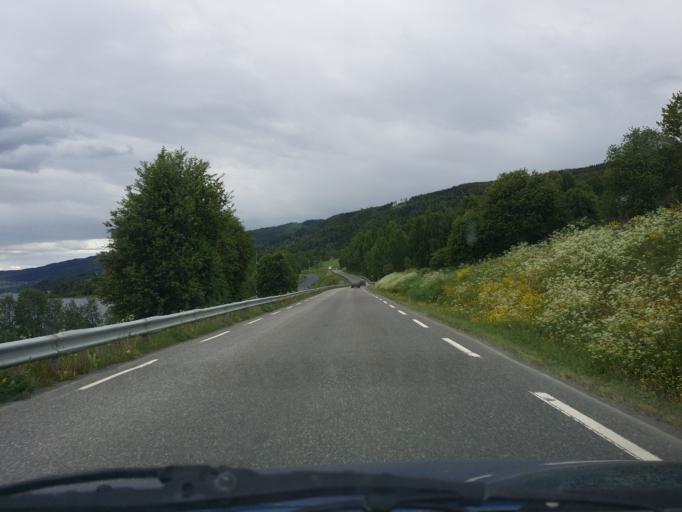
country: NO
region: Oppland
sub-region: Lillehammer
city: Lillehammer
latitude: 61.0339
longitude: 10.4411
